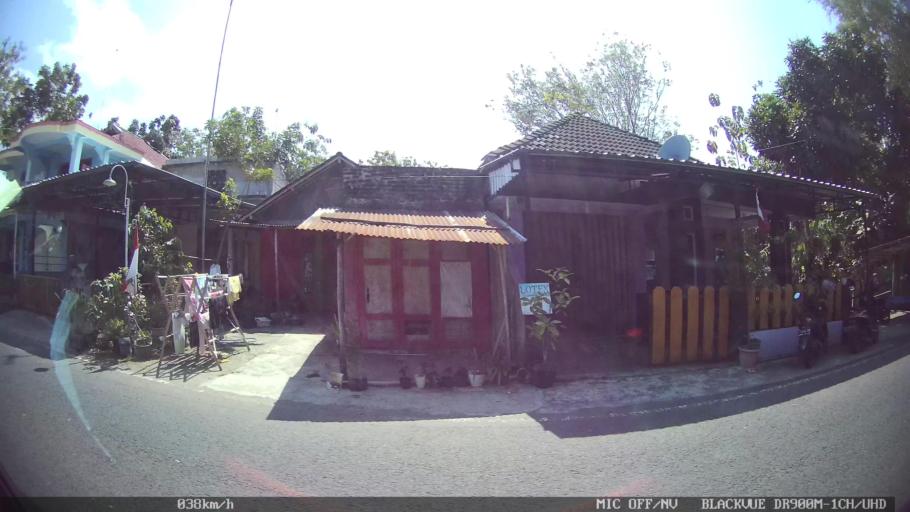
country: ID
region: Daerah Istimewa Yogyakarta
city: Pundong
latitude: -7.9598
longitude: 110.3580
